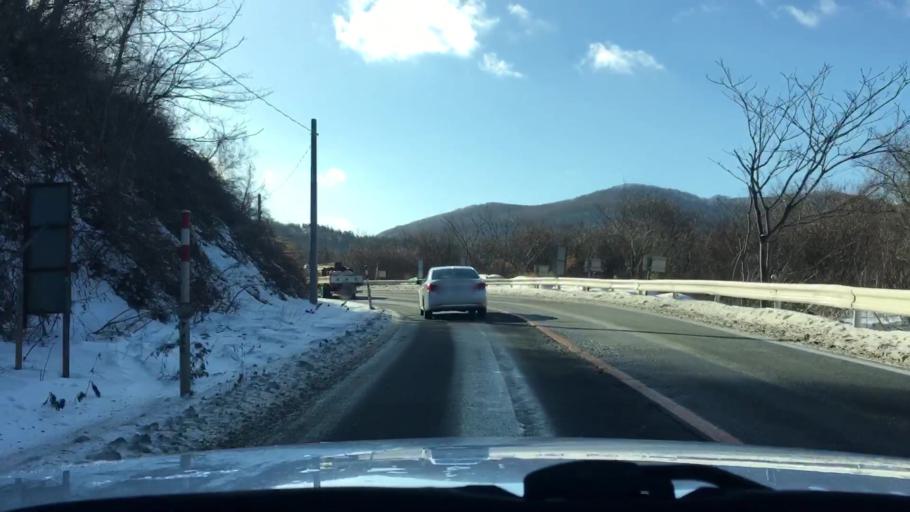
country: JP
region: Iwate
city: Morioka-shi
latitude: 39.6596
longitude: 141.3374
